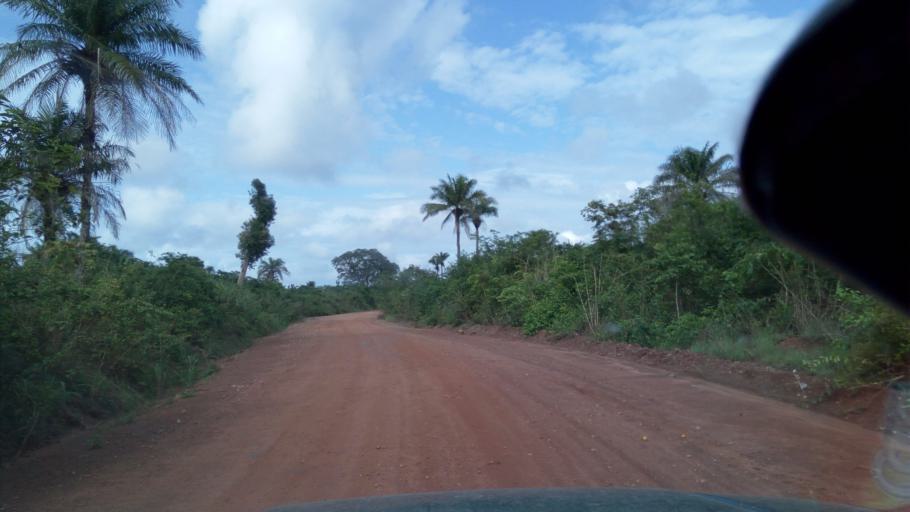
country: SL
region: Northern Province
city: Pepel
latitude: 8.6453
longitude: -13.0179
